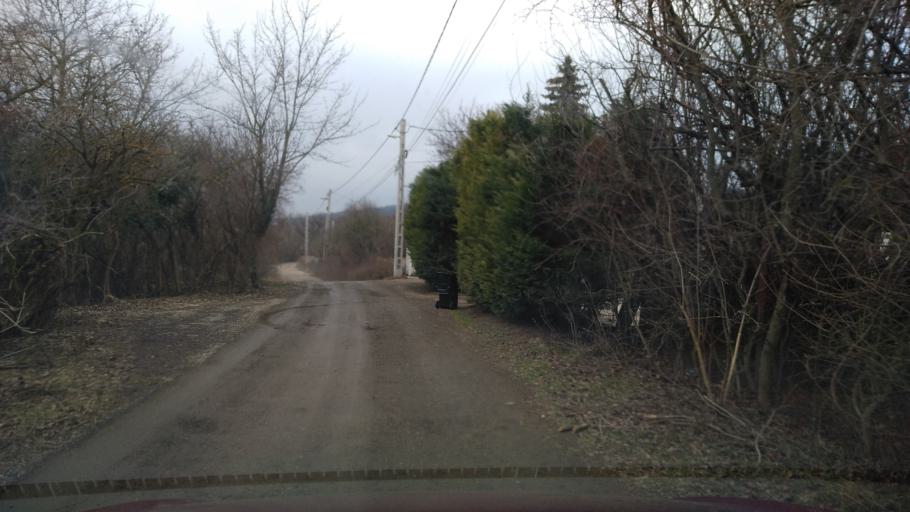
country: HU
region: Pest
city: Szentendre
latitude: 47.6946
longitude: 19.0519
